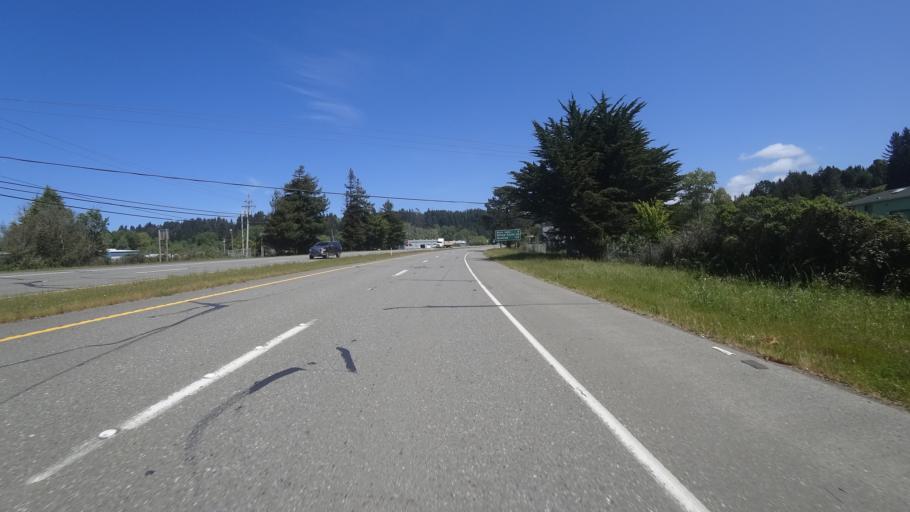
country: US
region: California
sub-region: Humboldt County
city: Arcata
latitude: 40.9081
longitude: -124.0722
